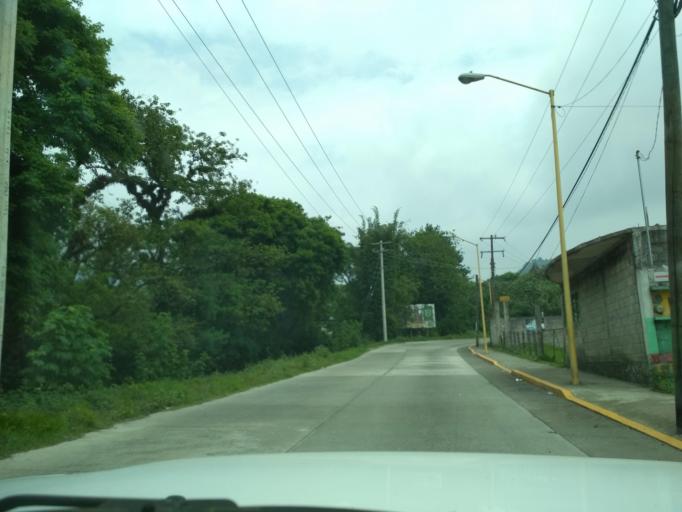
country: MX
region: Veracruz
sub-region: La Perla
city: La Perla
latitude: 18.9217
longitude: -97.1325
